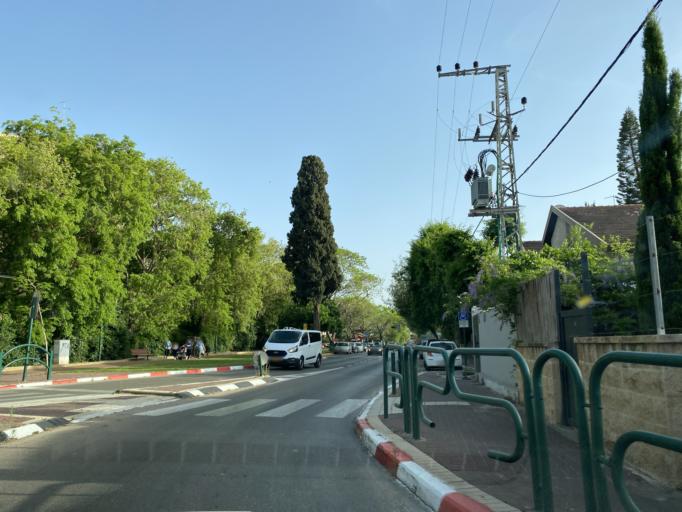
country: IL
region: Central District
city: Kfar Saba
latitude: 32.1809
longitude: 34.9098
